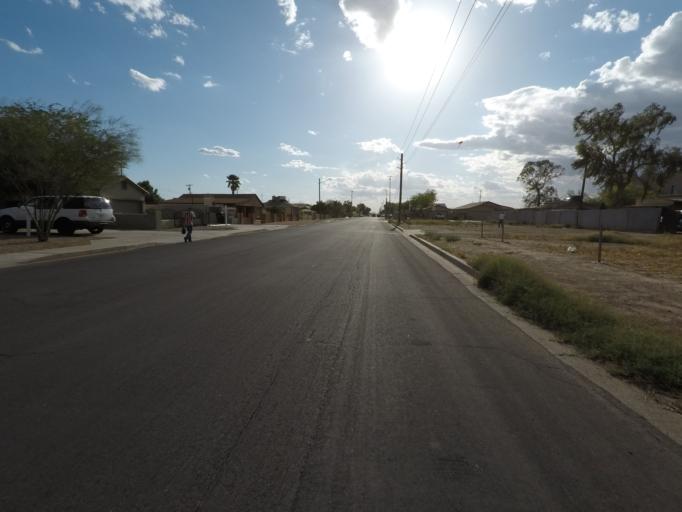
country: US
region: Arizona
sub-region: Maricopa County
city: Phoenix
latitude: 33.4332
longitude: -112.0850
